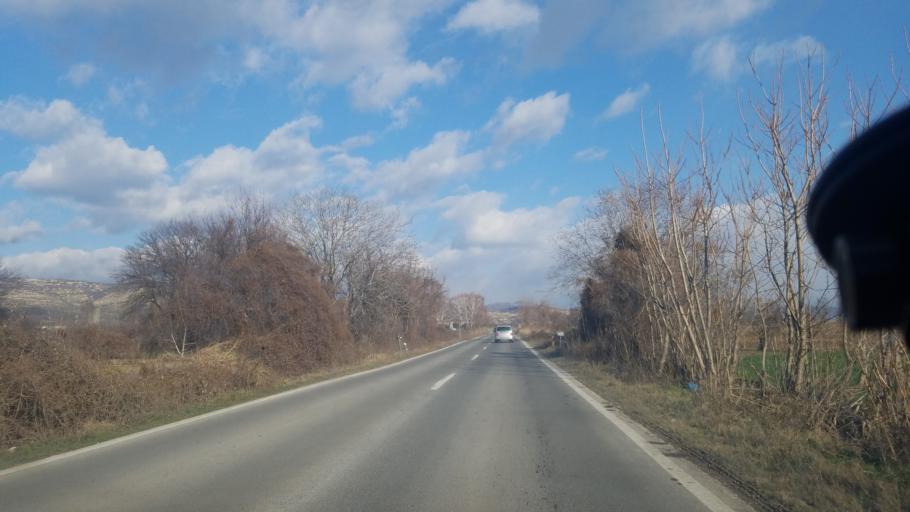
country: MK
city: Obleshevo
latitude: 41.8965
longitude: 22.3585
